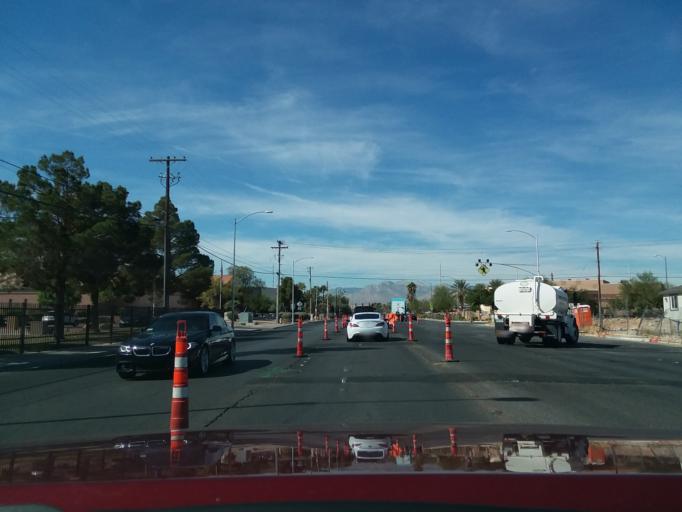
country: US
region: Nevada
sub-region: Clark County
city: Las Vegas
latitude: 36.1957
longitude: -115.1530
